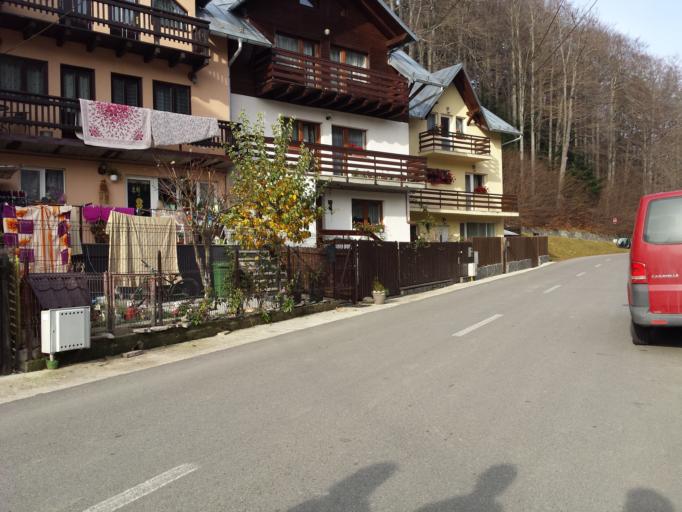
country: RO
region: Prahova
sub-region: Oras Busteni
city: Busteni
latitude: 45.4252
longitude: 25.5382
